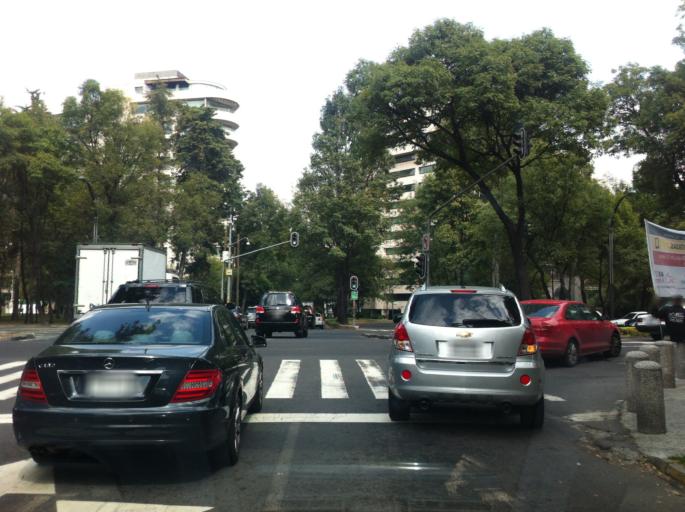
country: MX
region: Mexico City
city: Miguel Hidalgo
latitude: 19.4265
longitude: -99.1984
